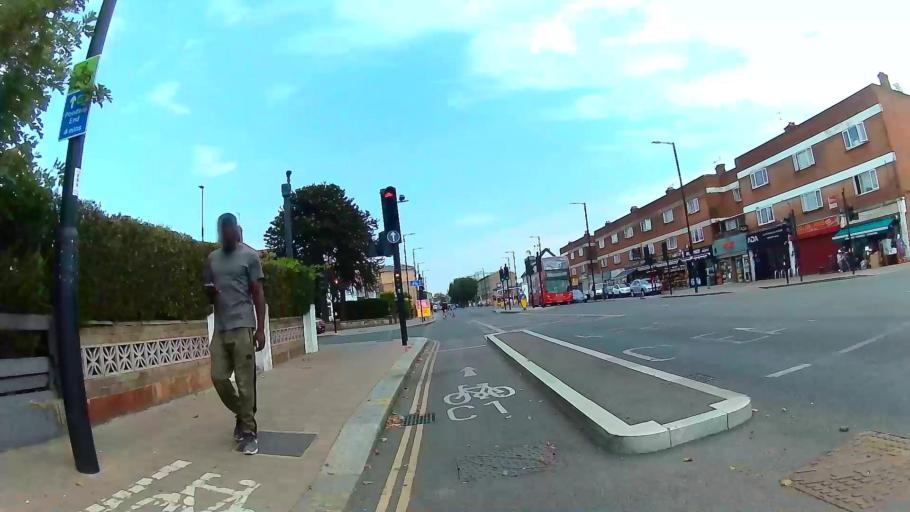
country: GB
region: England
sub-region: Greater London
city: Enfield
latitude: 51.6392
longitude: -0.0481
